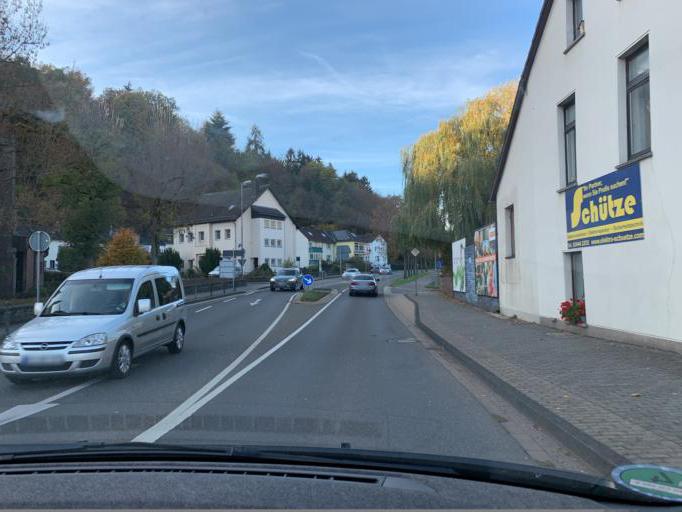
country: DE
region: North Rhine-Westphalia
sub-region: Regierungsbezirk Koln
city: Schleiden
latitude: 50.5719
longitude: 6.4999
